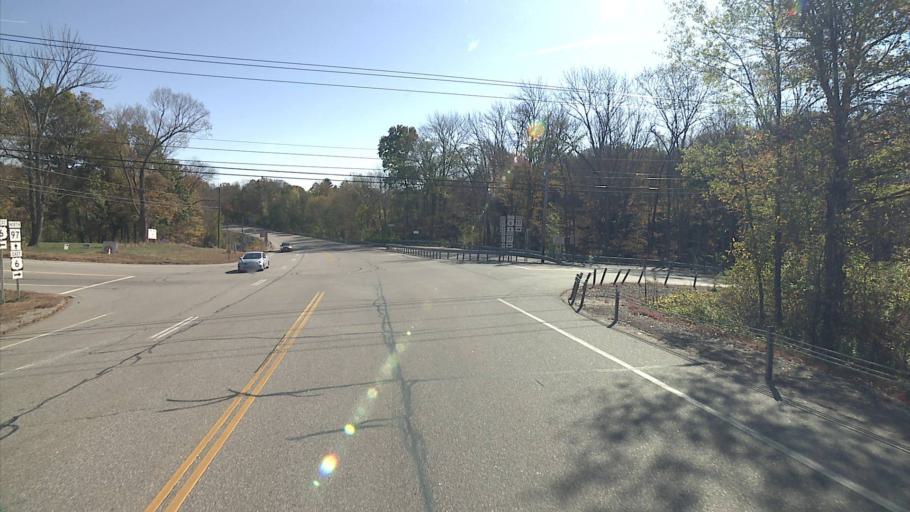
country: US
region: Connecticut
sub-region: Windham County
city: Windham
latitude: 41.7676
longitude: -72.0578
